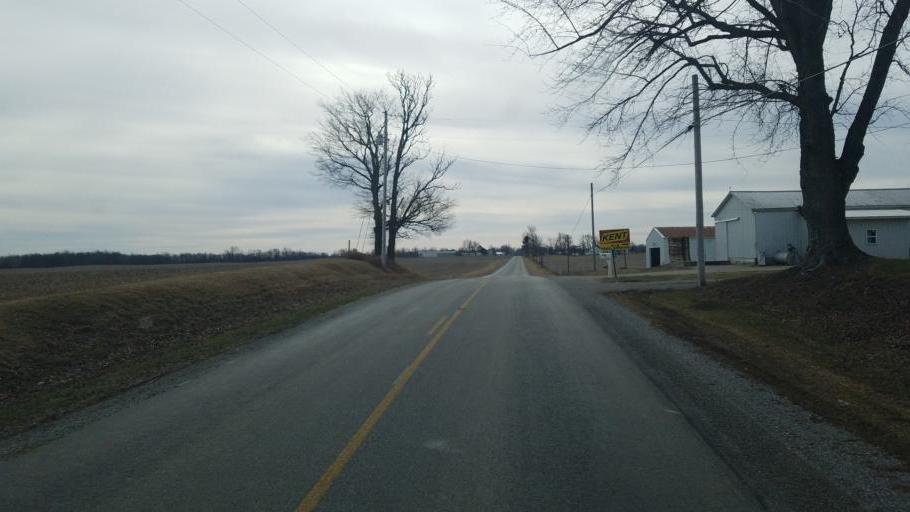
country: US
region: Ohio
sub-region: Hardin County
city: Kenton
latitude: 40.5498
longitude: -83.5133
